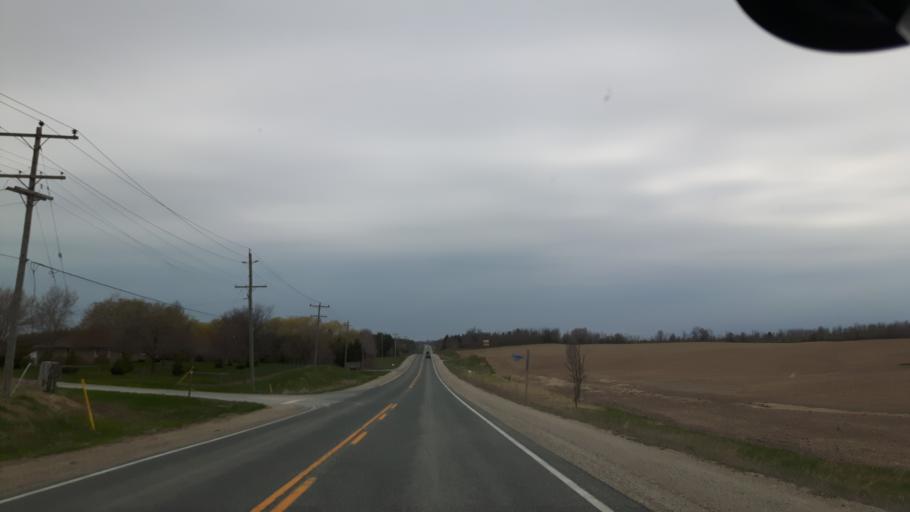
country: CA
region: Ontario
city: Goderich
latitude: 43.6610
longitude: -81.6182
